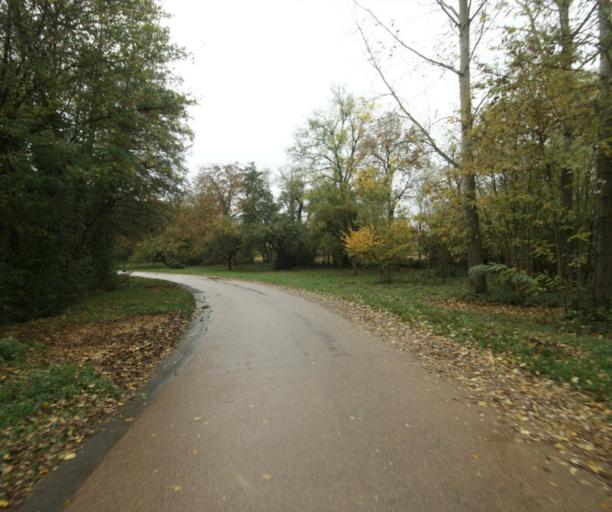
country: FR
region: Rhone-Alpes
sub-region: Departement de l'Ain
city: Pont-de-Vaux
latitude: 46.4748
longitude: 4.8799
